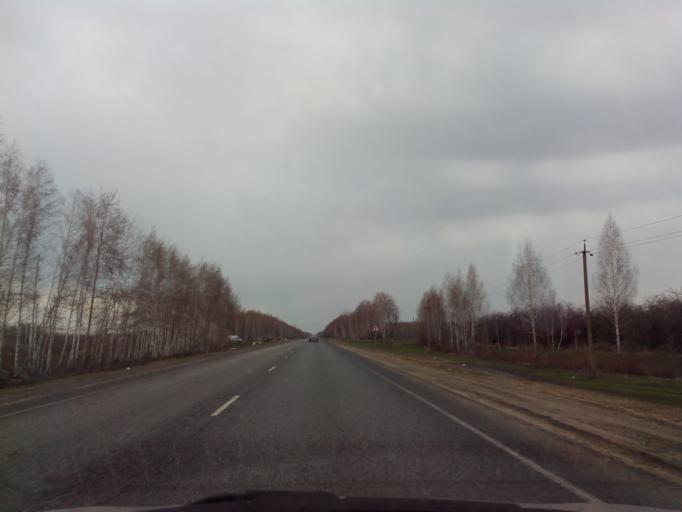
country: RU
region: Tambov
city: Michurinsk
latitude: 53.0473
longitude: 40.4756
